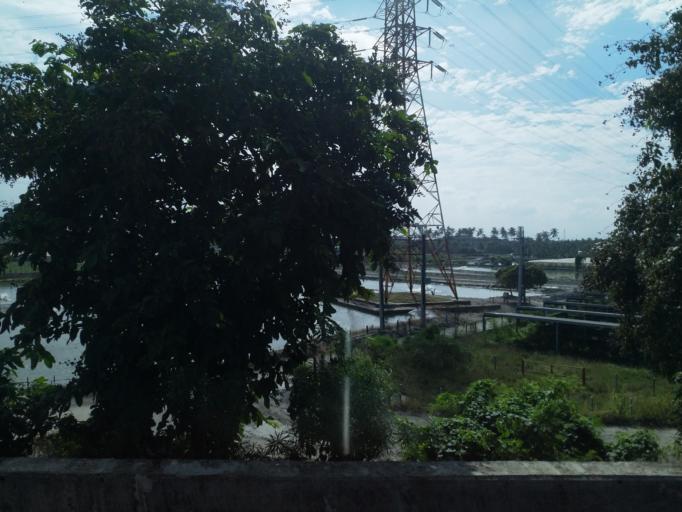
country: TW
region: Taiwan
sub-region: Pingtung
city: Pingtung
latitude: 22.8041
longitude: 120.4801
